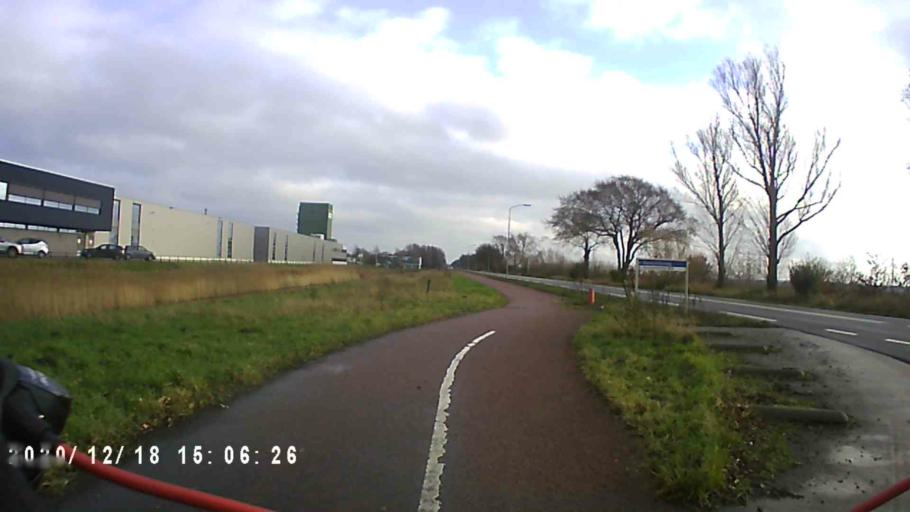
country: NL
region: Groningen
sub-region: Gemeente Hoogezand-Sappemeer
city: Hoogezand
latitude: 53.1724
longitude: 6.6868
